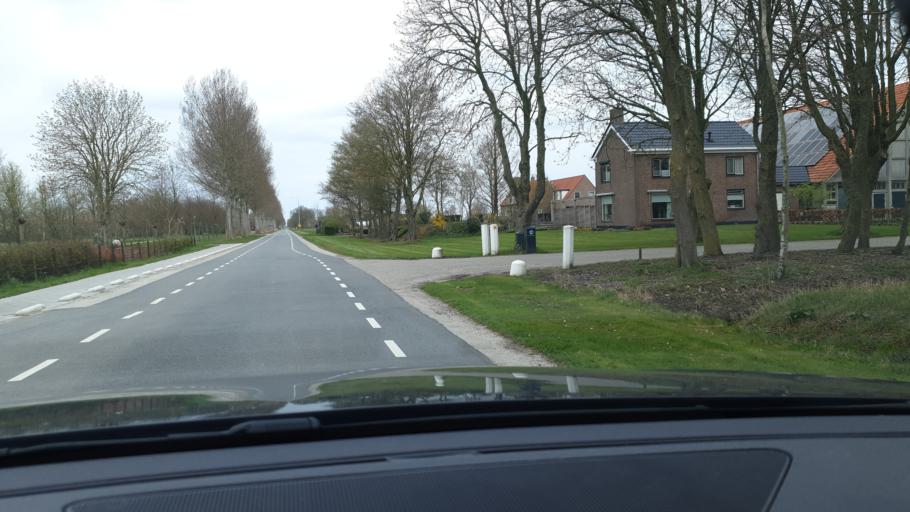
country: NL
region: Flevoland
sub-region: Gemeente Urk
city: Urk
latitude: 52.7252
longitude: 5.6406
